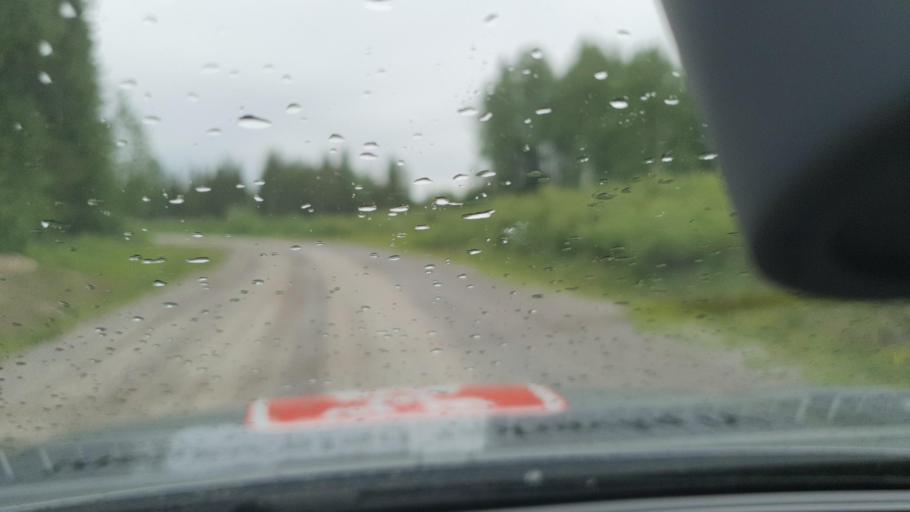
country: SE
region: Norrbotten
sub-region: Kalix Kommun
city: Rolfs
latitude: 66.0655
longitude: 22.9968
